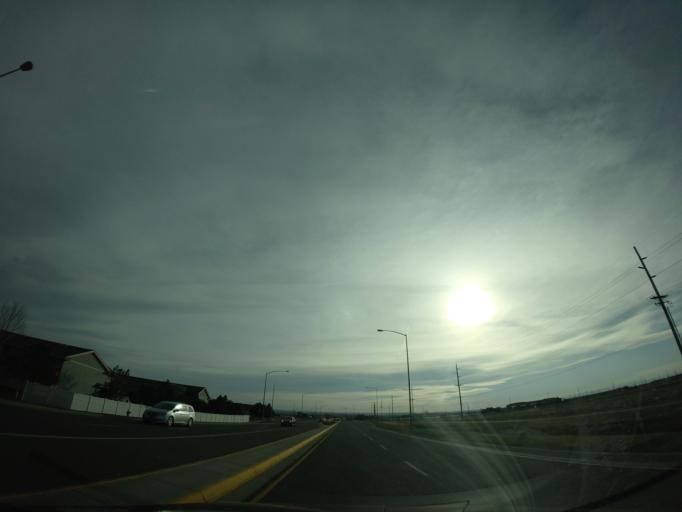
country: US
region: Montana
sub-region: Yellowstone County
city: Billings
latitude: 45.7577
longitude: -108.6177
